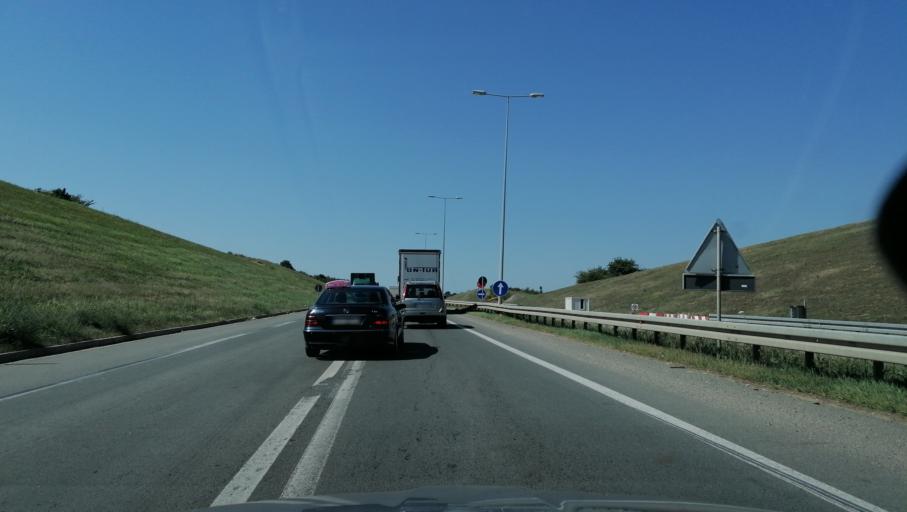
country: RS
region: Central Serbia
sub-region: Belgrade
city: Rakovica
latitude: 44.7171
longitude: 20.4383
